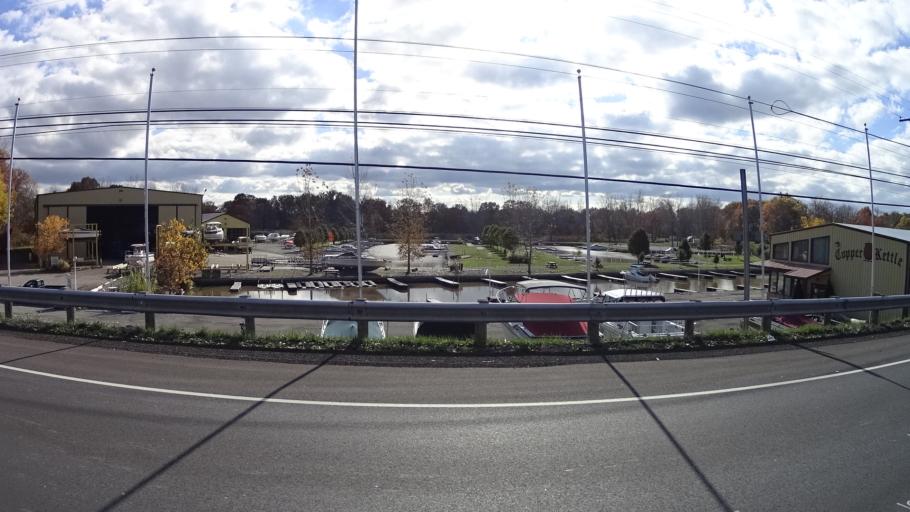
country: US
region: Ohio
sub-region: Lorain County
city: Amherst
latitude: 41.4377
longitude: -82.2445
